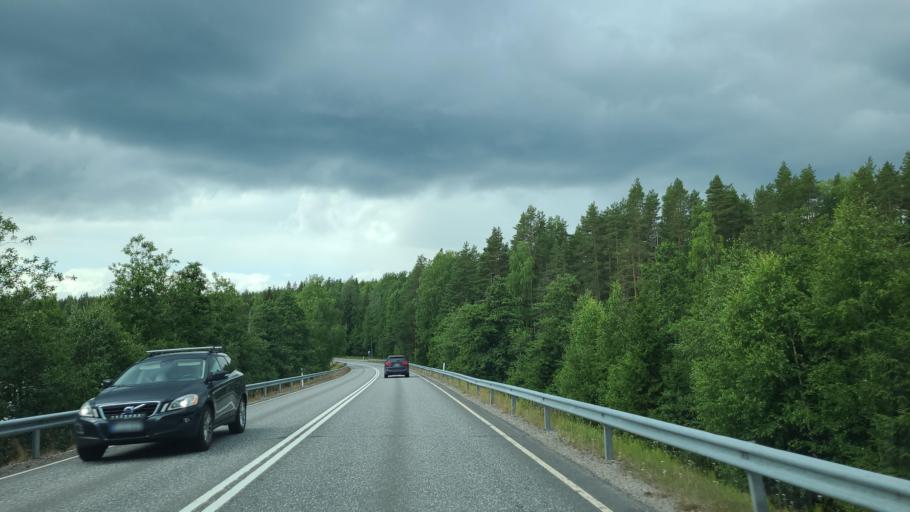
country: FI
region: Northern Savo
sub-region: Sisae-Savo
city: Rautalampi
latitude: 62.5404
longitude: 26.9289
